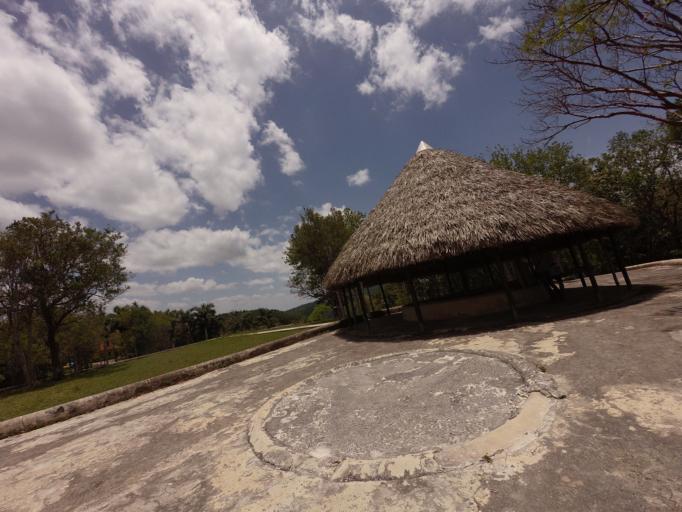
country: CU
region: Artemisa
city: Soroa
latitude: 22.8628
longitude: -82.9284
